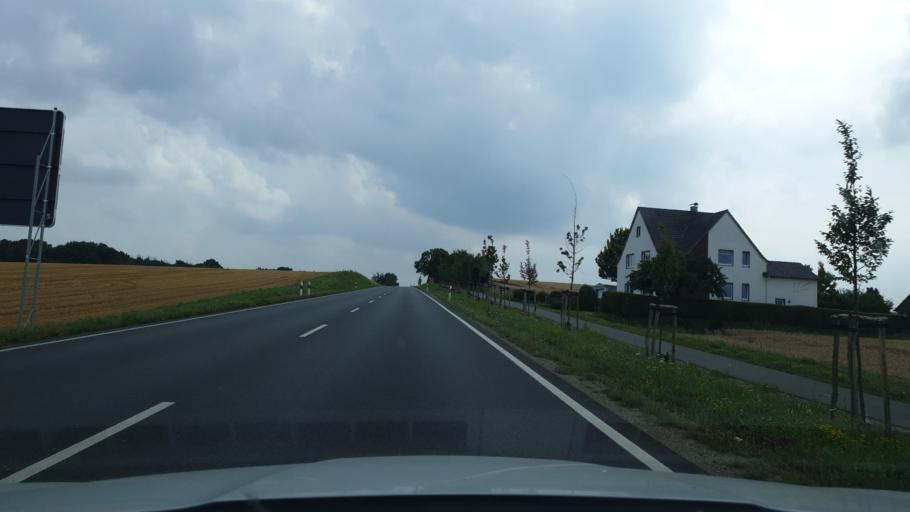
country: DE
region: North Rhine-Westphalia
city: Loehne
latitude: 52.1715
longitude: 8.7491
